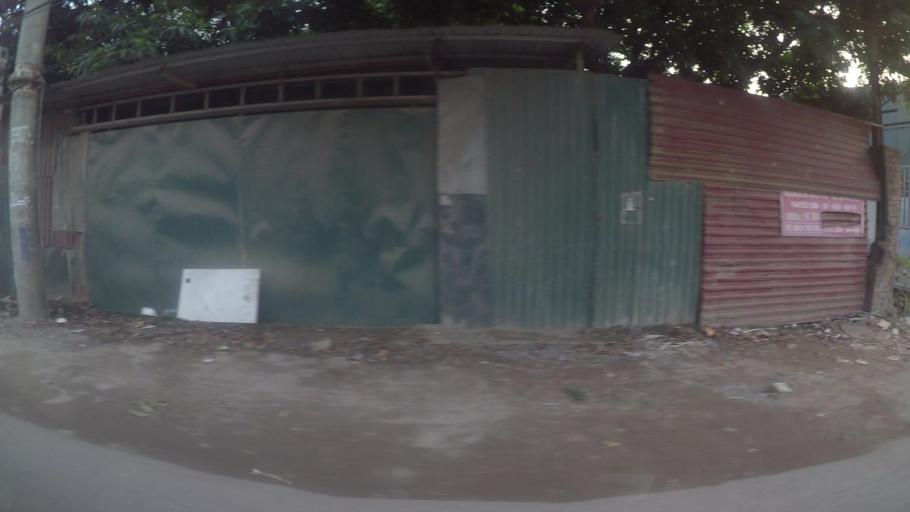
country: VN
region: Ha Noi
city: Tay Ho
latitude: 21.0747
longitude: 105.7980
